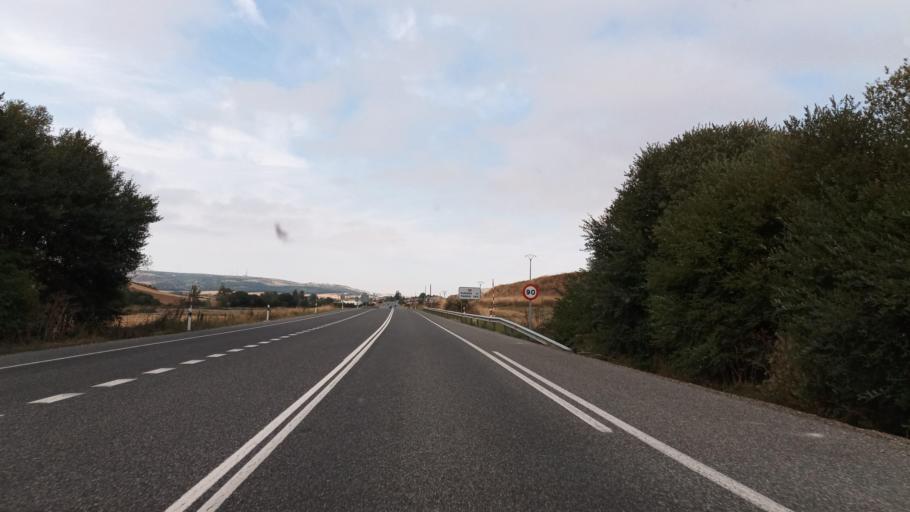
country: ES
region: Castille and Leon
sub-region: Provincia de Burgos
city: Quintanapalla
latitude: 42.4215
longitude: -3.5149
